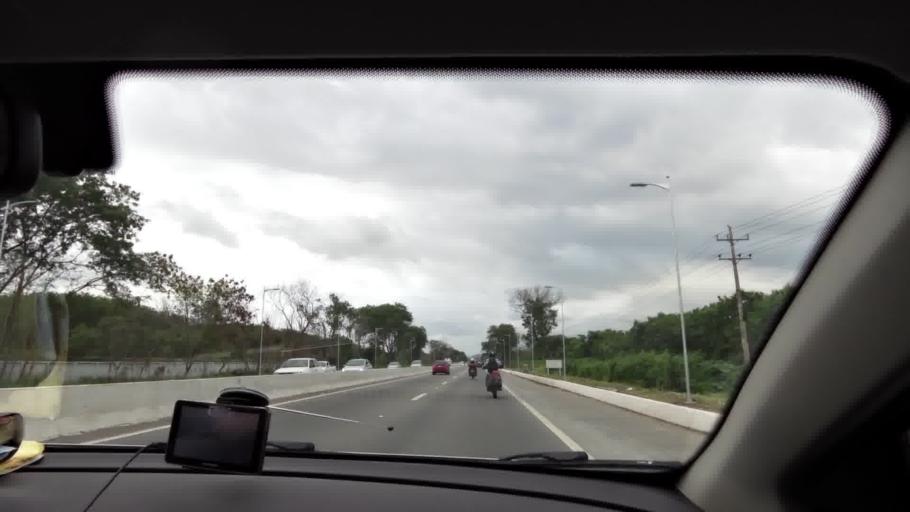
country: BR
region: Espirito Santo
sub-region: Vila Velha
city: Vila Velha
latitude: -20.2455
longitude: -40.2831
